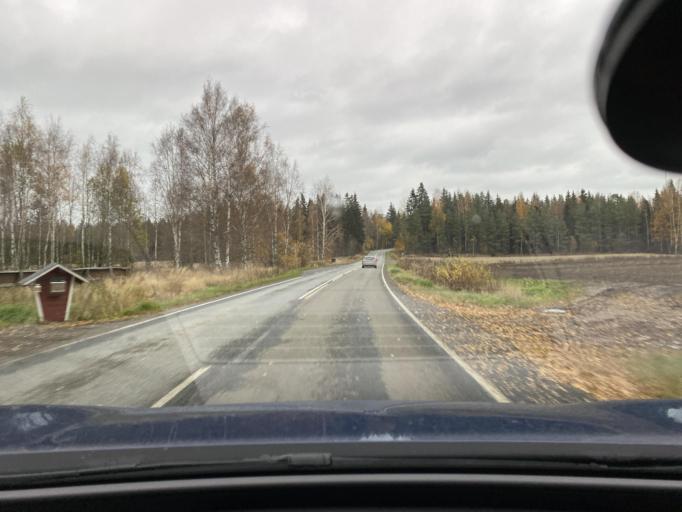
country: FI
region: Satakunta
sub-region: Pori
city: Vampula
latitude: 61.0971
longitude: 22.5423
